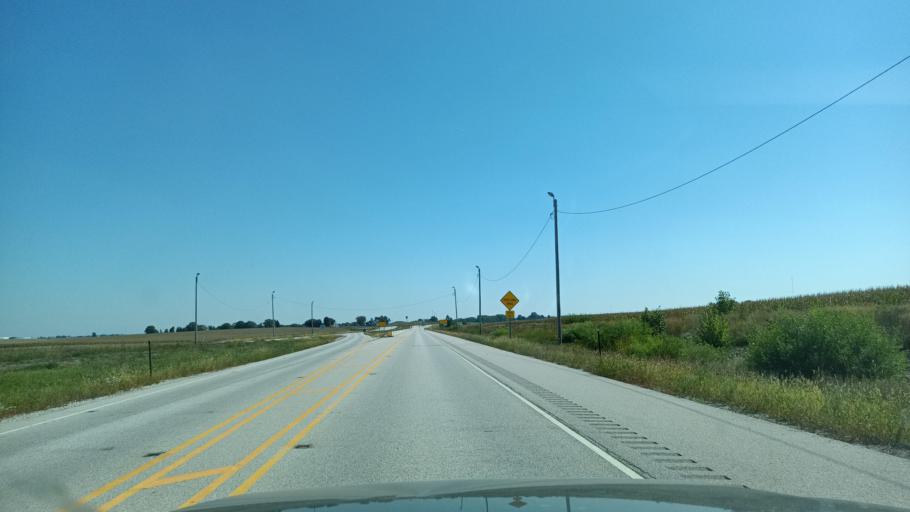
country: US
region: Illinois
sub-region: McDonough County
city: Macomb
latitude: 40.5032
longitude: -90.6876
